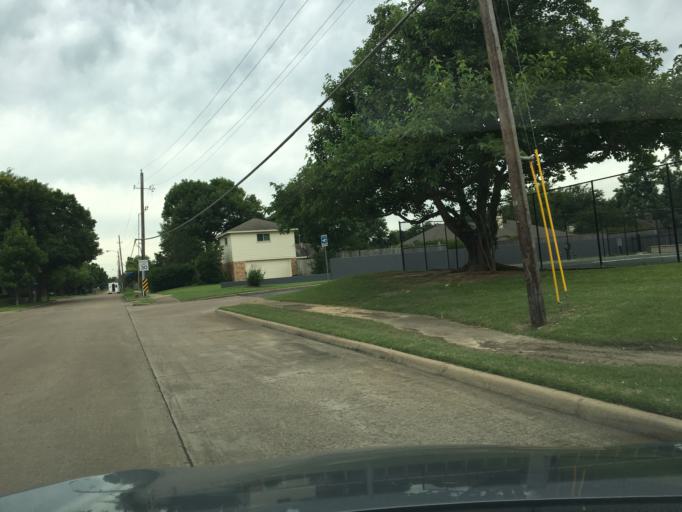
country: US
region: Texas
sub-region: Dallas County
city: Richardson
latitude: 32.9450
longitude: -96.7098
